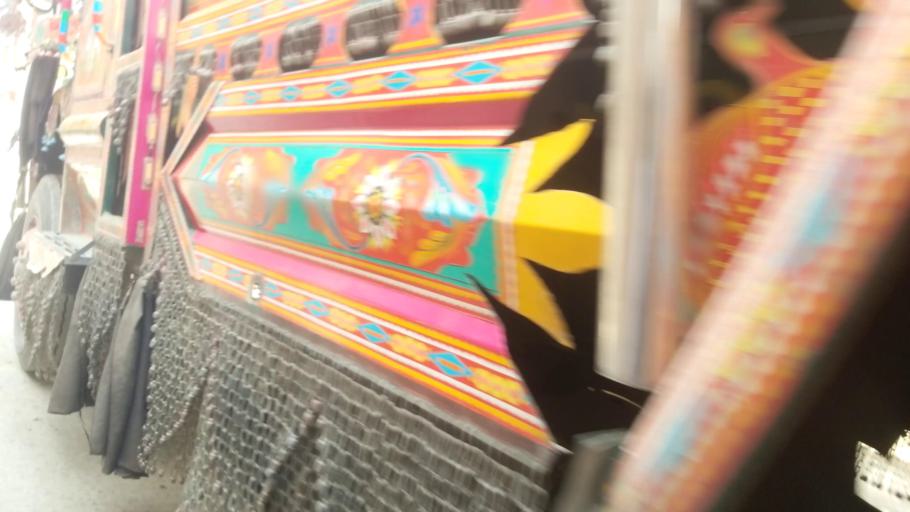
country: PK
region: Khyber Pakhtunkhwa
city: Peshawar
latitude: 33.9838
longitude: 71.5335
